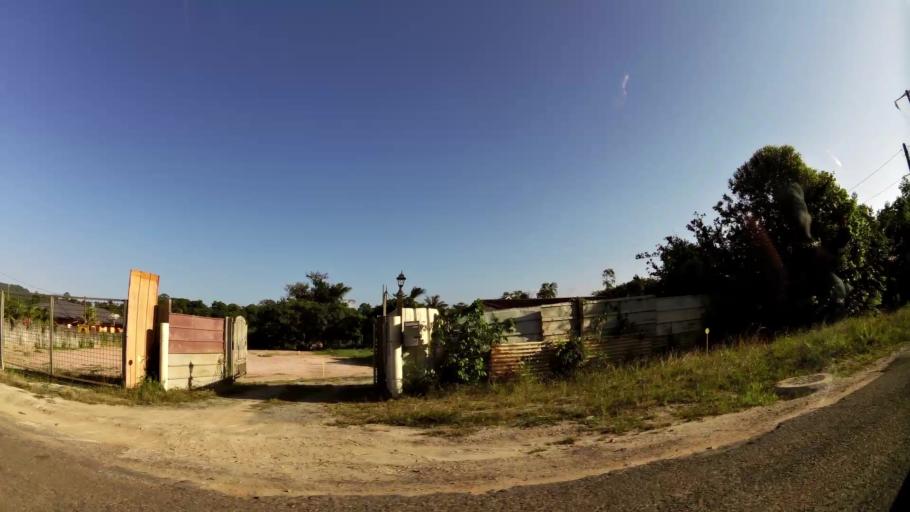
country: GF
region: Guyane
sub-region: Guyane
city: Remire-Montjoly
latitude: 4.8885
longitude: -52.2919
